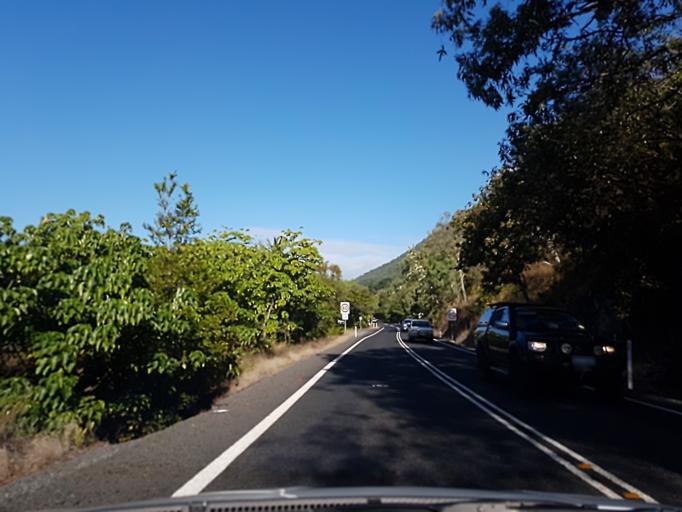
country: AU
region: Queensland
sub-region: Cairns
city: Palm Cove
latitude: -16.7206
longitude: 145.6412
